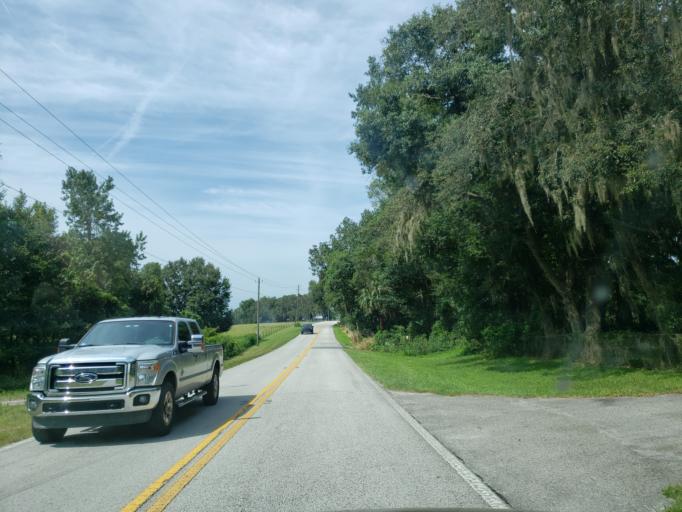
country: US
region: Florida
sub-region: Pasco County
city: San Antonio
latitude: 28.3791
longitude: -82.2869
